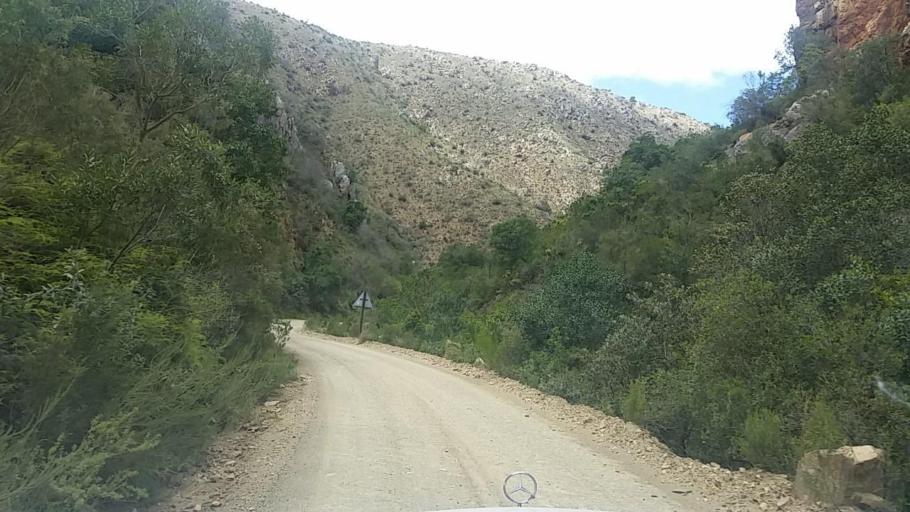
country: ZA
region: Western Cape
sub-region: Eden District Municipality
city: Knysna
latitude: -33.8033
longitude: 23.1803
